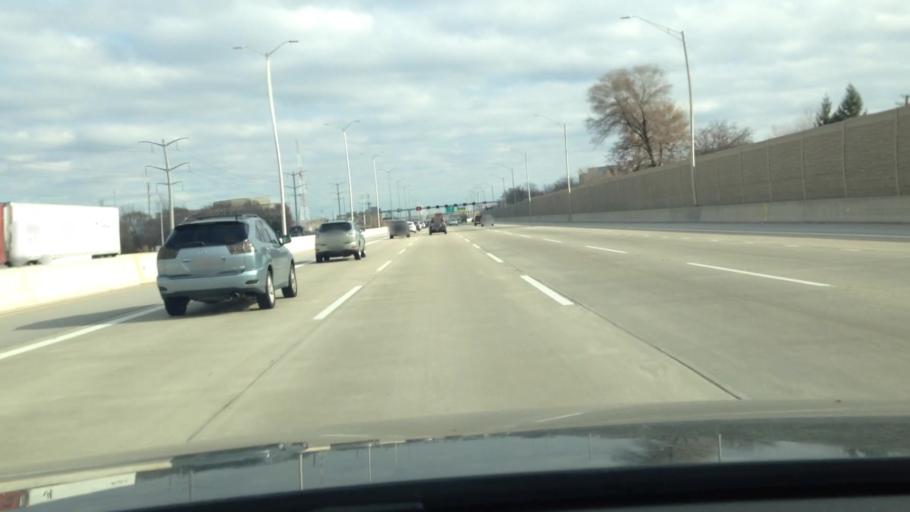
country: US
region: Illinois
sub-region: Cook County
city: Hoffman Estates
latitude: 42.0674
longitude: -88.0925
